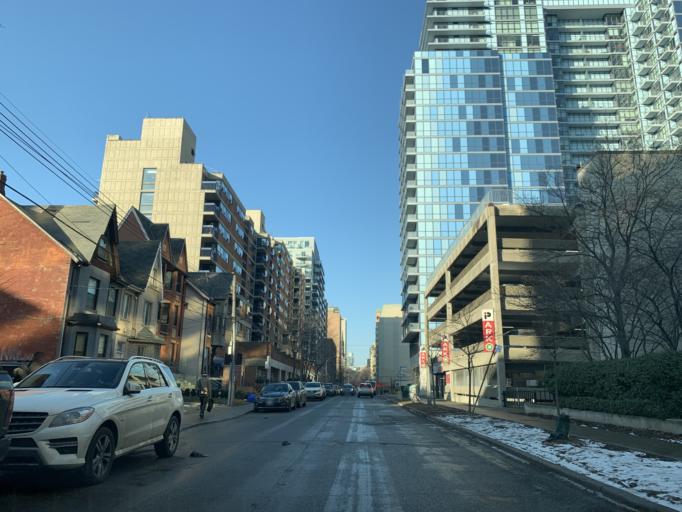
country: CA
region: Ontario
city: Toronto
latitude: 43.6515
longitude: -79.3891
